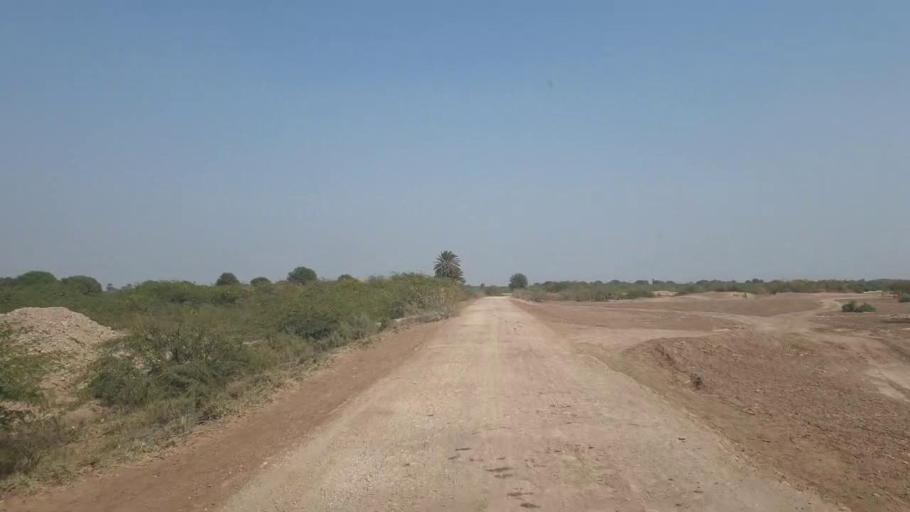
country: PK
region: Sindh
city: Mirpur Khas
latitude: 25.4435
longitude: 68.8888
